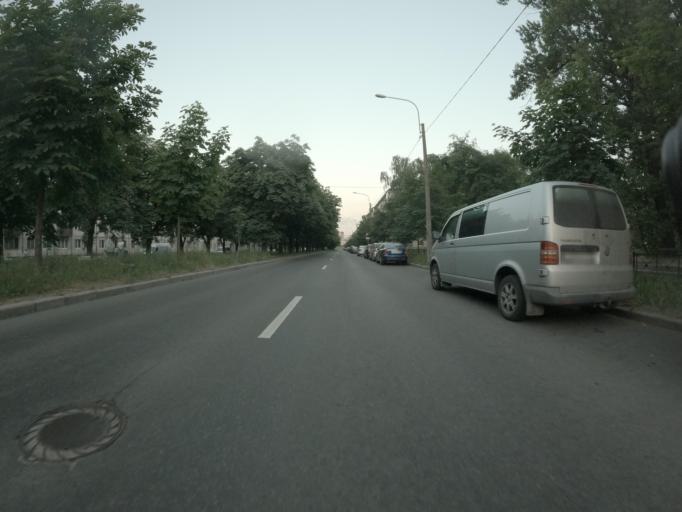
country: RU
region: St.-Petersburg
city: Centralniy
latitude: 59.9244
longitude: 30.4241
